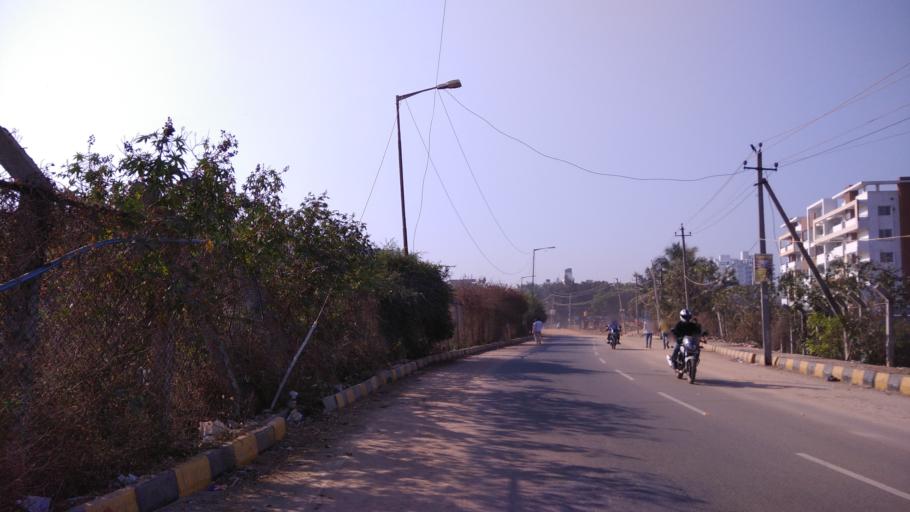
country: IN
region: Karnataka
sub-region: Bangalore Rural
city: Hoskote
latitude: 12.9737
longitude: 77.7345
